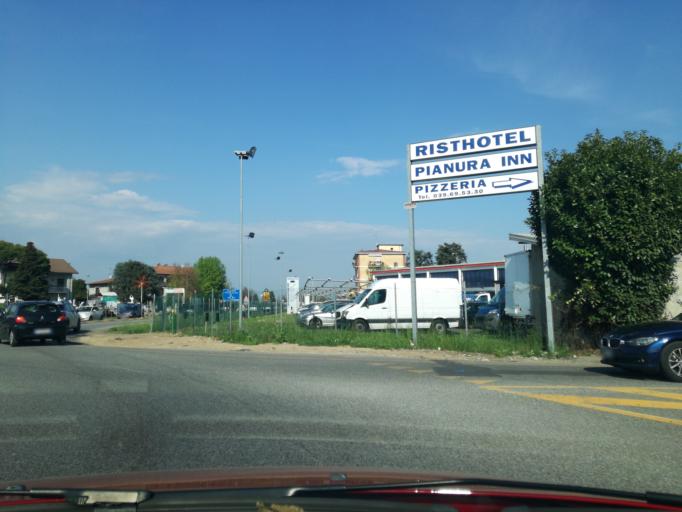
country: IT
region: Lombardy
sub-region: Provincia di Monza e Brianza
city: Busnago
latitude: 45.6172
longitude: 9.4529
